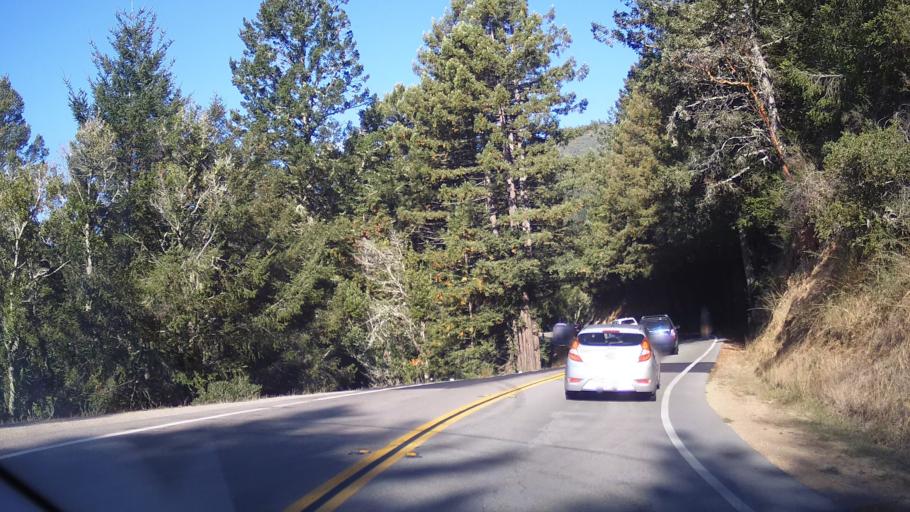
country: US
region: California
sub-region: Marin County
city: Mill Valley
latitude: 37.9125
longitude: -122.5803
